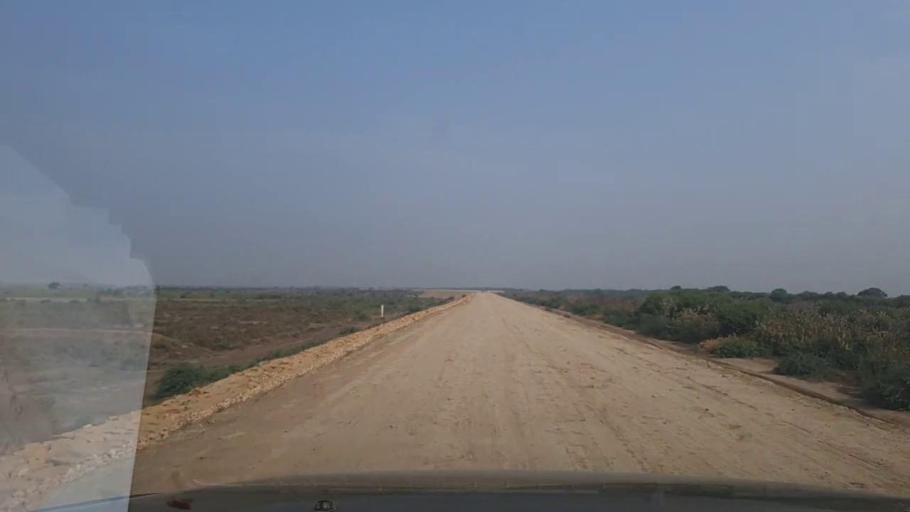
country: PK
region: Sindh
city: Bulri
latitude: 24.9516
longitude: 68.2903
